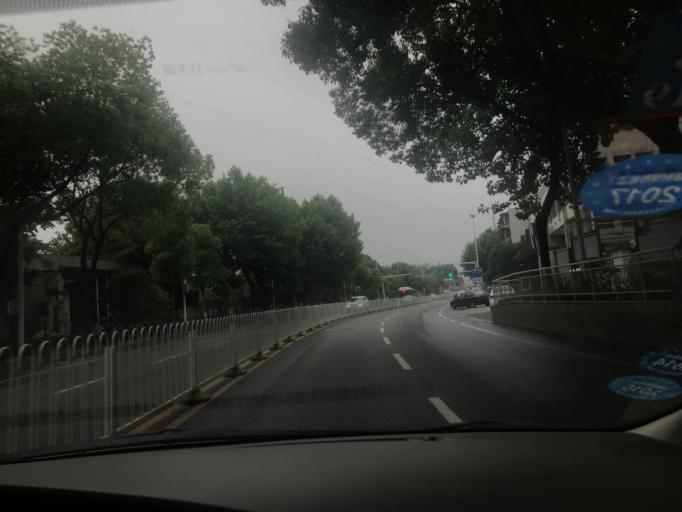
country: CN
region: Hubei
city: Wuhan
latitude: 30.5519
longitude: 114.2716
